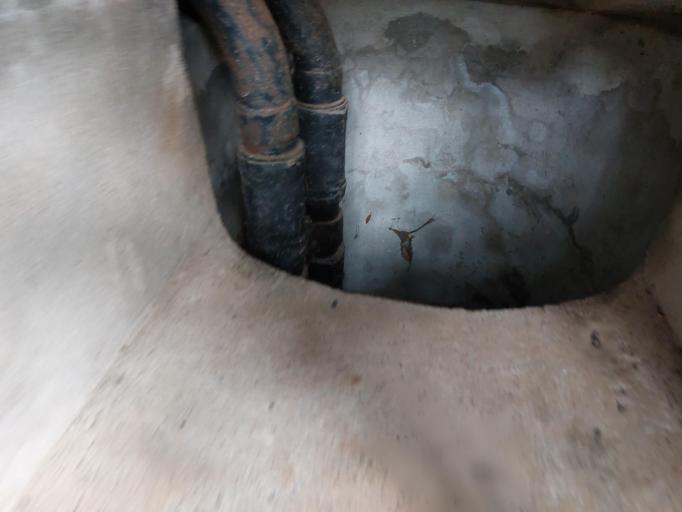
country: HR
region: Dubrovacko-Neretvanska
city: Smokvica
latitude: 42.7630
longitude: 16.8129
